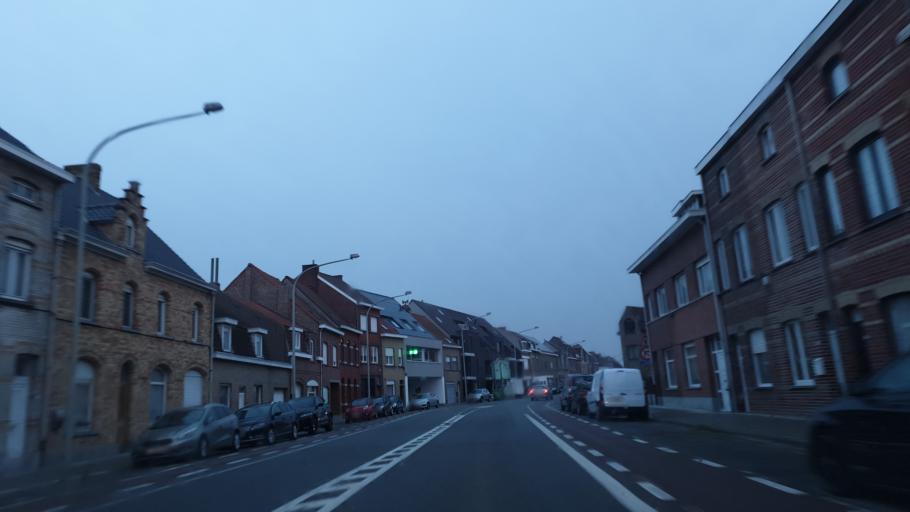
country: BE
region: Flanders
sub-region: Provincie West-Vlaanderen
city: Ieper
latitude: 50.8573
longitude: 2.8717
